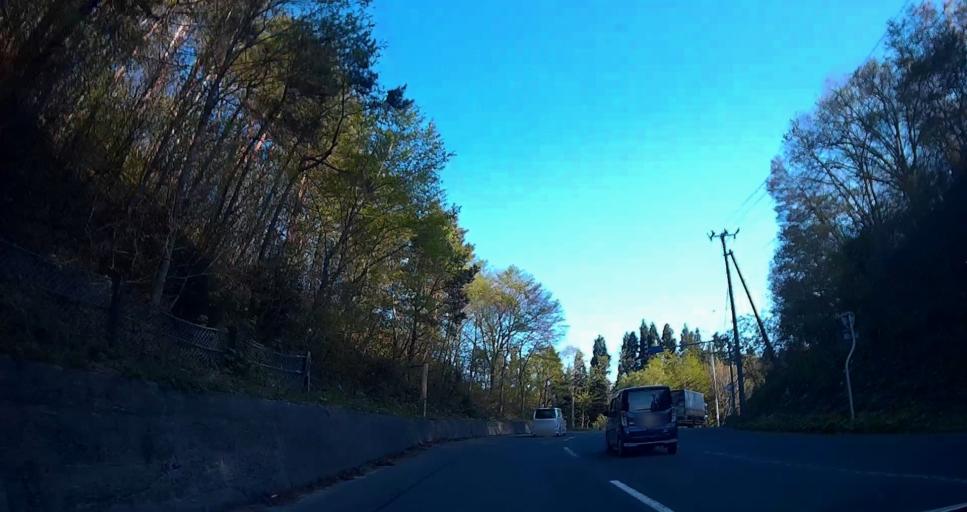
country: JP
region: Aomori
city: Mutsu
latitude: 41.4323
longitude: 141.1374
